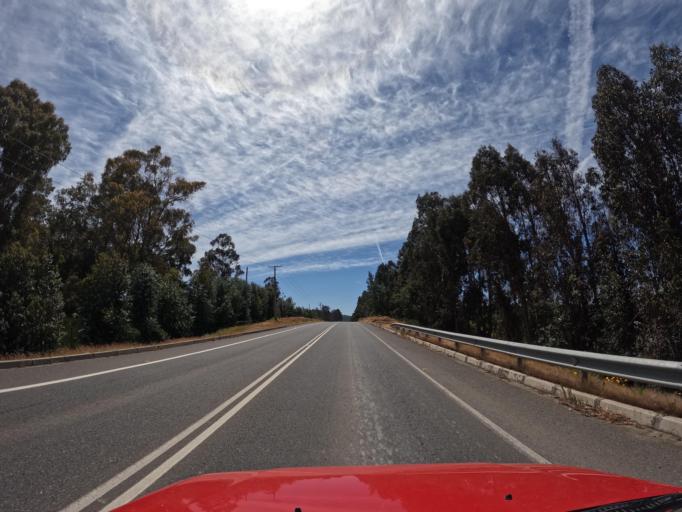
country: CL
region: Maule
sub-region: Provincia de Talca
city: Talca
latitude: -35.2889
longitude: -71.5310
